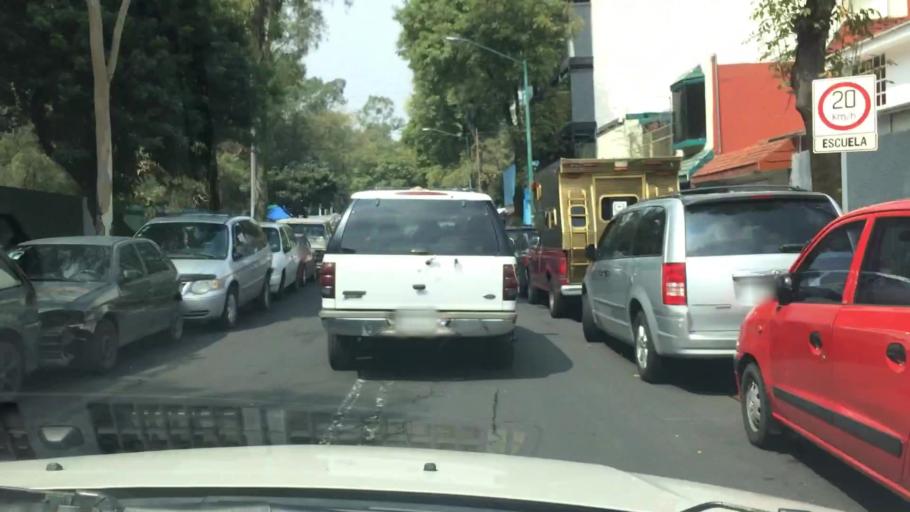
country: MX
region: Mexico City
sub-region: Iztacalco
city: Iztacalco
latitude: 19.4116
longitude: -99.1061
